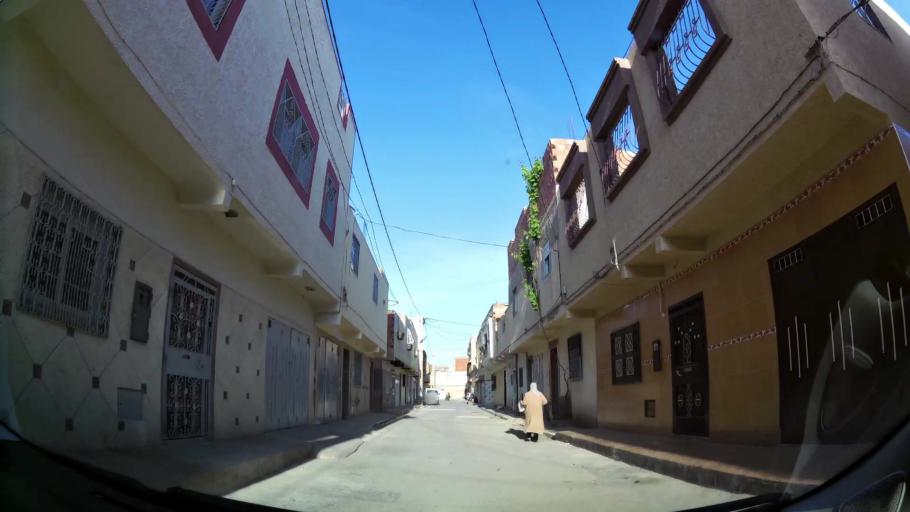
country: MA
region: Oriental
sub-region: Oujda-Angad
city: Oujda
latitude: 34.7086
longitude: -1.8959
